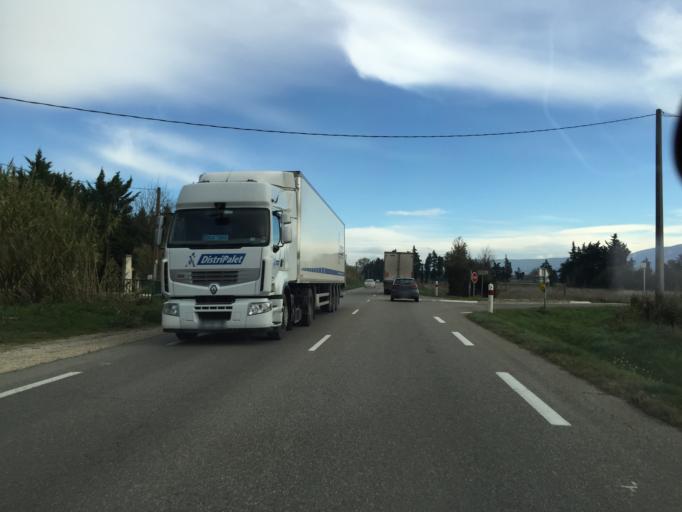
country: FR
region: Provence-Alpes-Cote d'Azur
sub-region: Departement du Vaucluse
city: Lagnes
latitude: 43.8724
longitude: 5.1039
